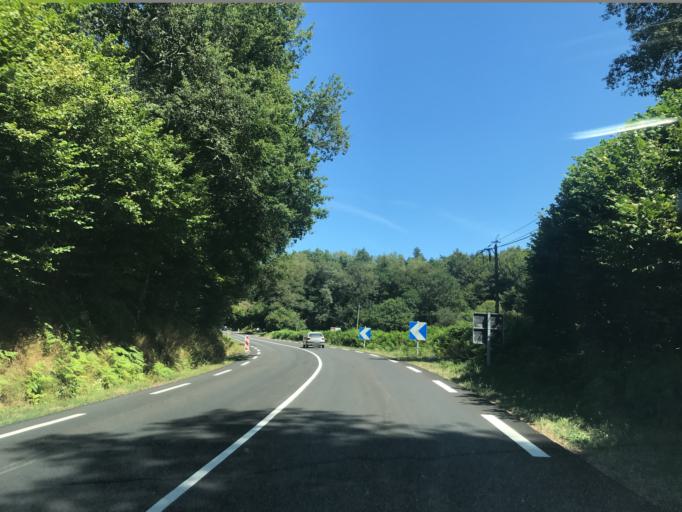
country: FR
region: Limousin
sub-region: Departement de la Correze
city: Egletons
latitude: 45.3877
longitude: 2.0281
